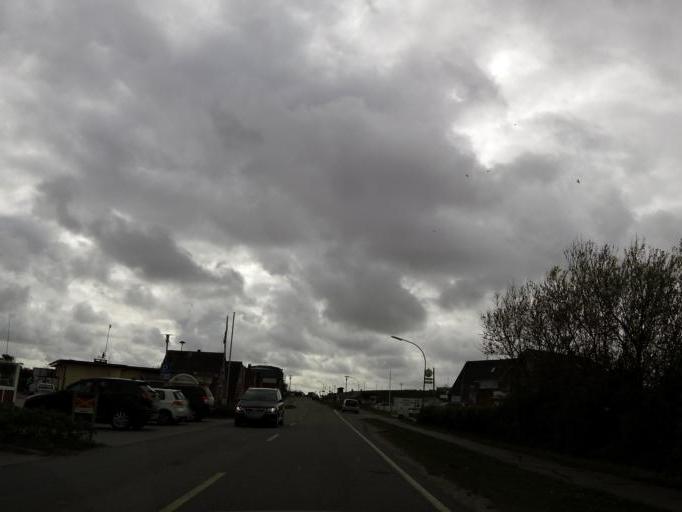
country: DE
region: Schleswig-Holstein
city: Dagebull
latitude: 54.7298
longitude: 8.6970
